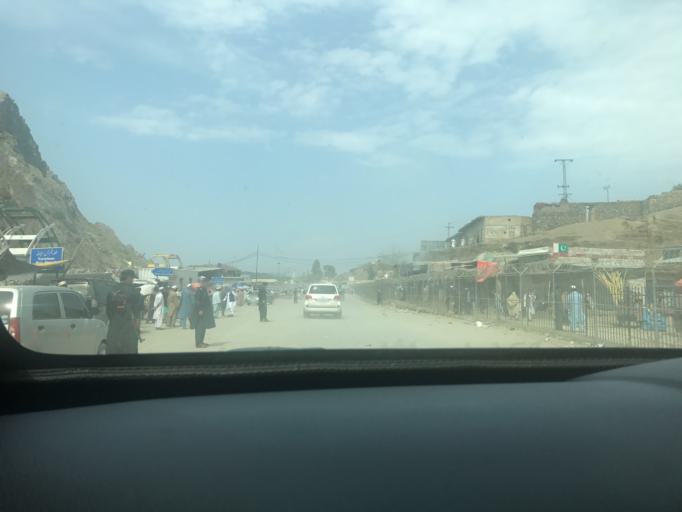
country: PK
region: Federally Administered Tribal Areas
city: Landi Kotal
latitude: 34.1190
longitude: 71.0989
